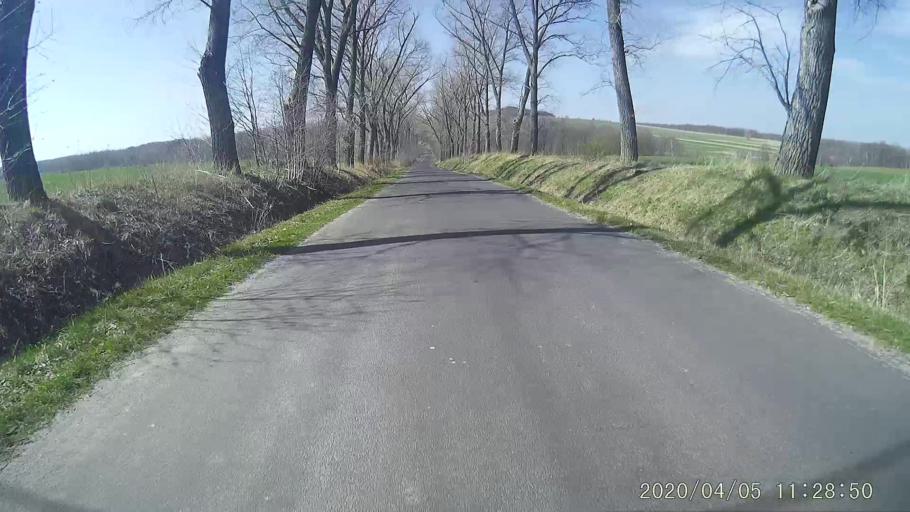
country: PL
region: Lower Silesian Voivodeship
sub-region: Powiat lubanski
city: Siekierczyn
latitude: 51.0606
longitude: 15.1644
